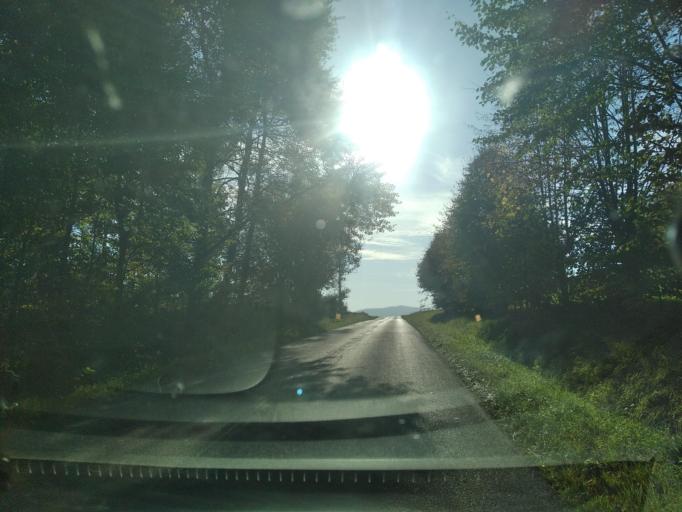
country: PL
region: Subcarpathian Voivodeship
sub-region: Powiat sanocki
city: Besko
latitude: 49.5787
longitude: 21.9497
